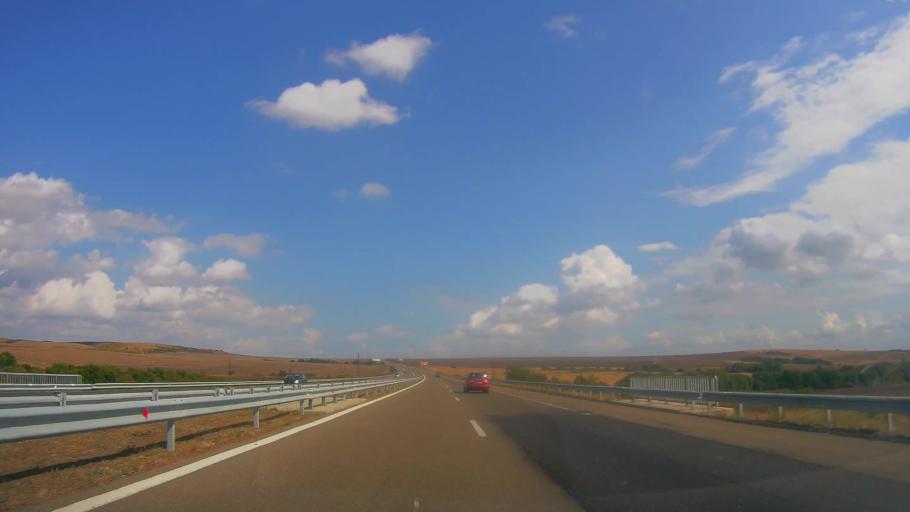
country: BG
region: Burgas
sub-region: Obshtina Karnobat
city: Karnobat
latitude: 42.5869
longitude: 27.0913
